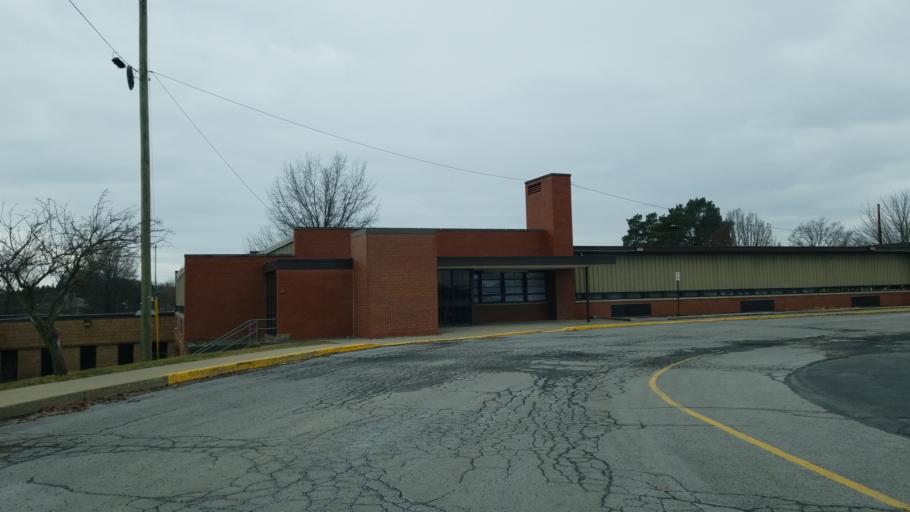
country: US
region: Pennsylvania
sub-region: Clearfield County
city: DuBois
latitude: 41.1135
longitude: -78.7387
